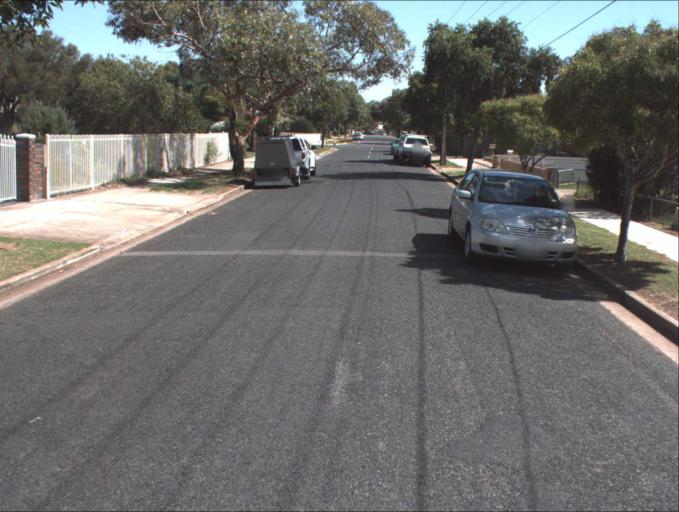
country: AU
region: South Australia
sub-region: Port Adelaide Enfield
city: Klemzig
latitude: -34.8800
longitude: 138.6455
